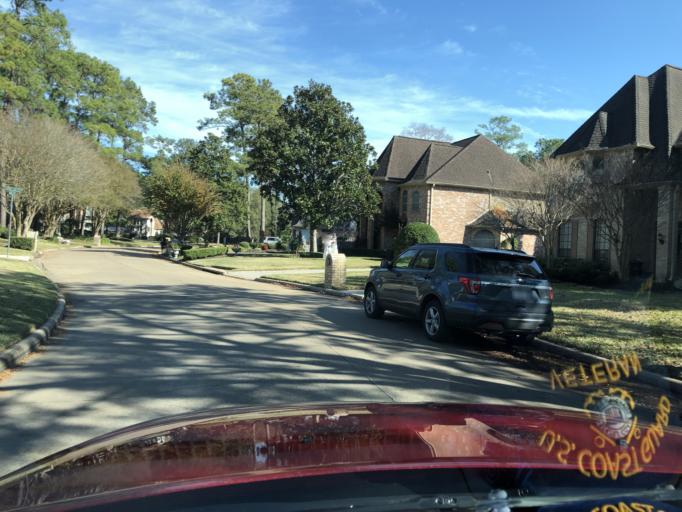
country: US
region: Texas
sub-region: Harris County
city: Tomball
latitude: 30.0190
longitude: -95.5482
